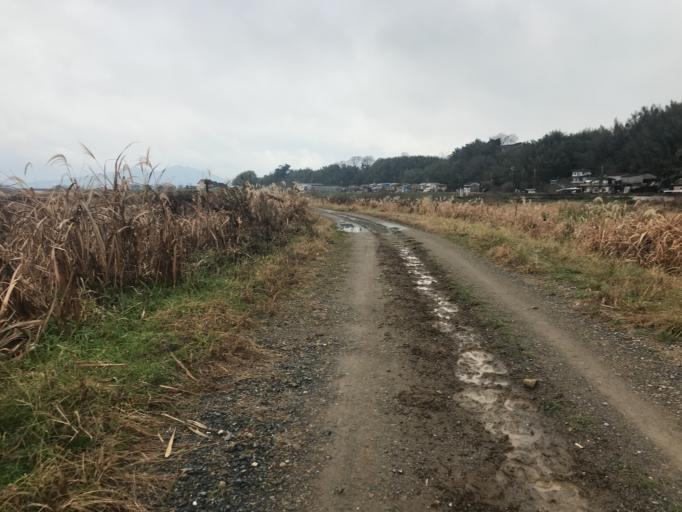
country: JP
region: Kyoto
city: Kameoka
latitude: 35.0180
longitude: 135.5993
